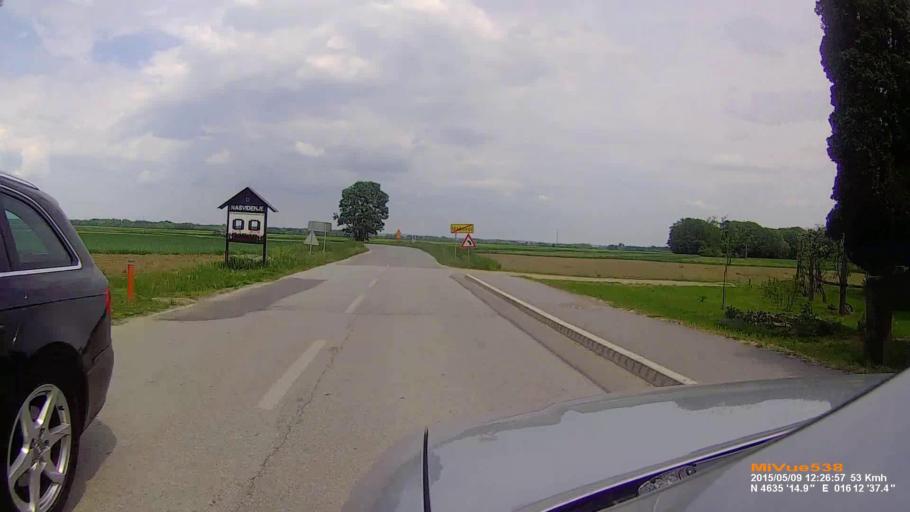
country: SI
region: Beltinci
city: Beltinci
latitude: 46.5875
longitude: 16.2104
